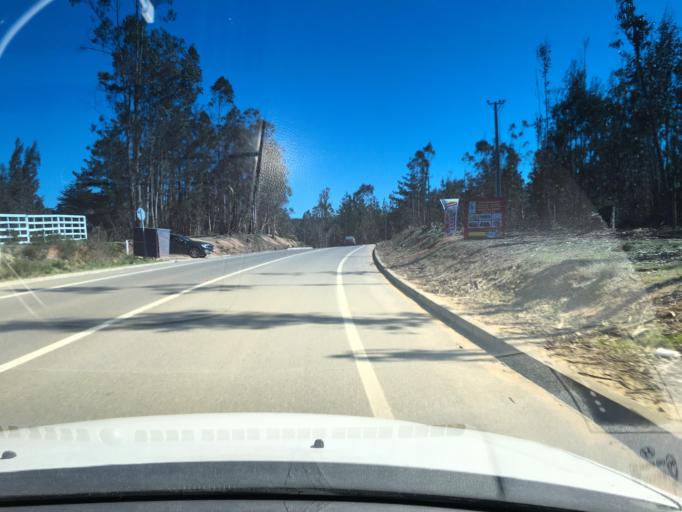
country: CL
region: Valparaiso
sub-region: San Antonio Province
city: El Tabo
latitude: -33.4249
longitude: -71.6336
